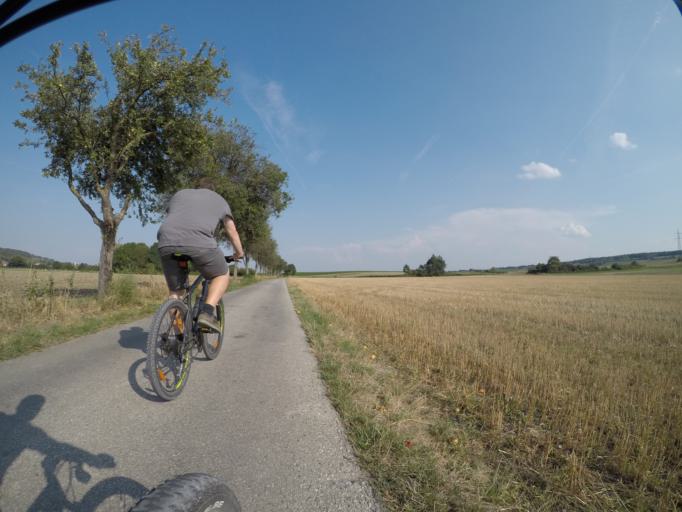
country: AT
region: Lower Austria
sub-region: Politischer Bezirk Baden
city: Hirtenberg
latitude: 47.9568
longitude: 16.1797
